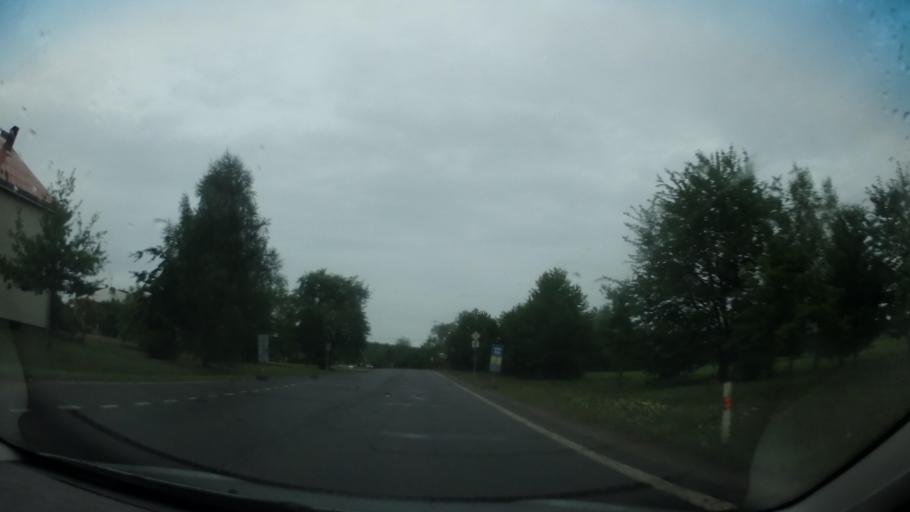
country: CZ
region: Central Bohemia
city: Milovice
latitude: 50.2317
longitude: 14.8879
